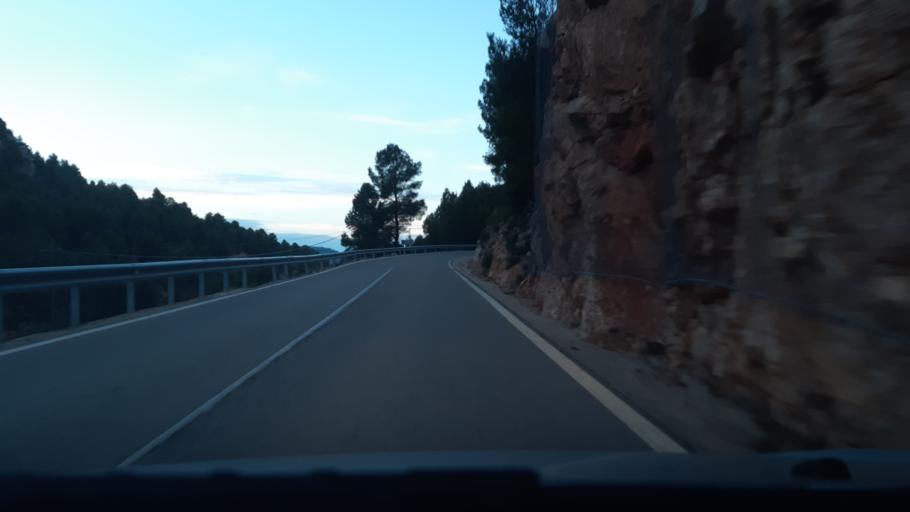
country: ES
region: Aragon
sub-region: Provincia de Teruel
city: Valderrobres
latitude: 40.8440
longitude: 0.1752
